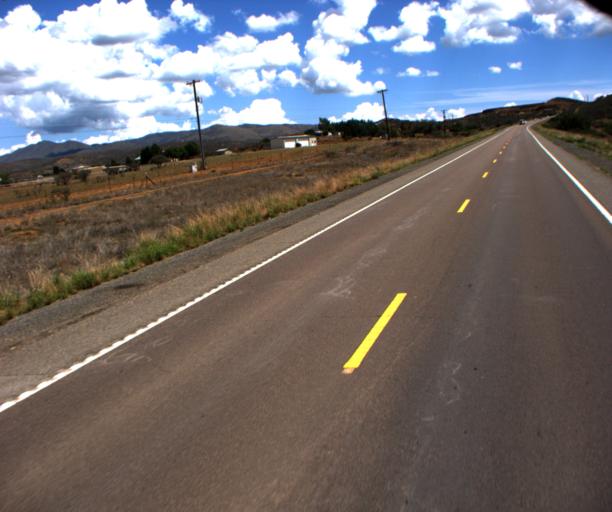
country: US
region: Arizona
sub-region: Yavapai County
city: Dewey-Humboldt
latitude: 34.5358
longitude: -112.2113
